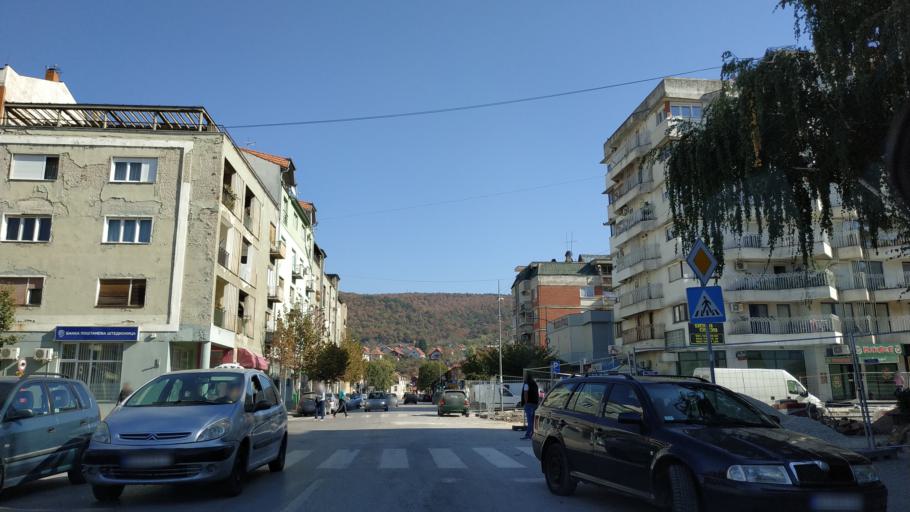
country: RS
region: Central Serbia
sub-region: Nisavski Okrug
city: Aleksinac
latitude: 43.5404
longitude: 21.7087
